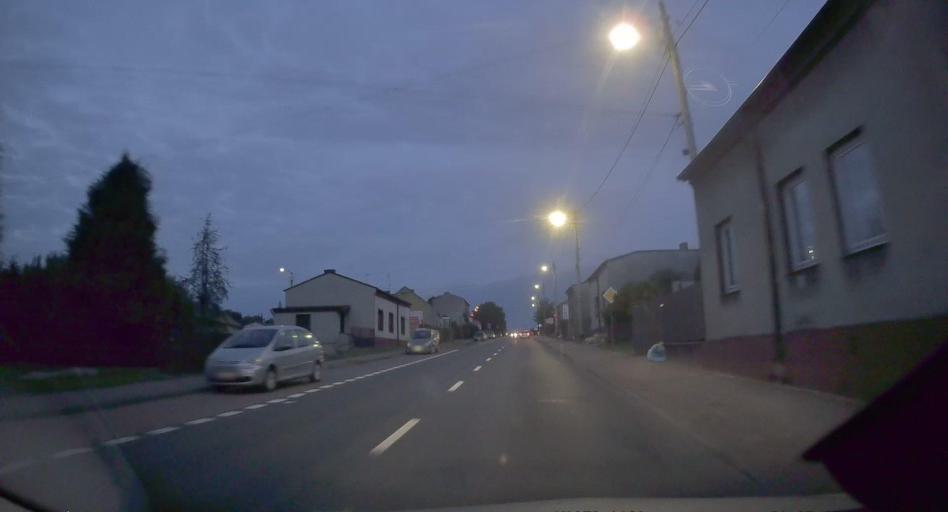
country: PL
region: Silesian Voivodeship
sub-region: Powiat klobucki
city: Klobuck
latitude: 50.9000
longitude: 18.9390
